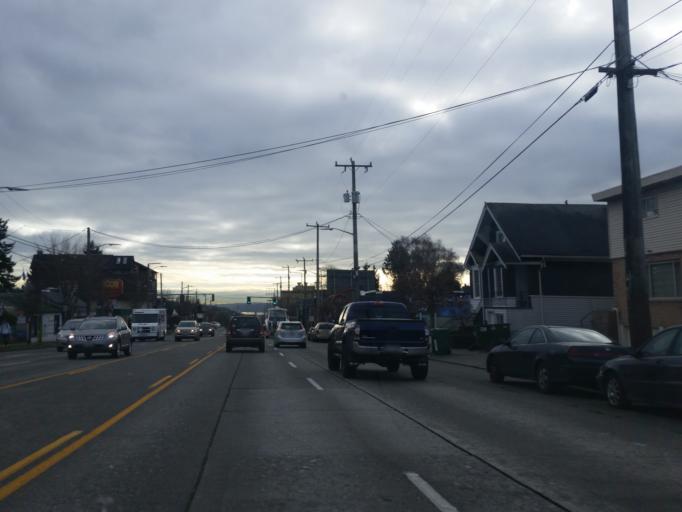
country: US
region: Washington
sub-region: King County
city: Shoreline
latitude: 47.6844
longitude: -122.3768
